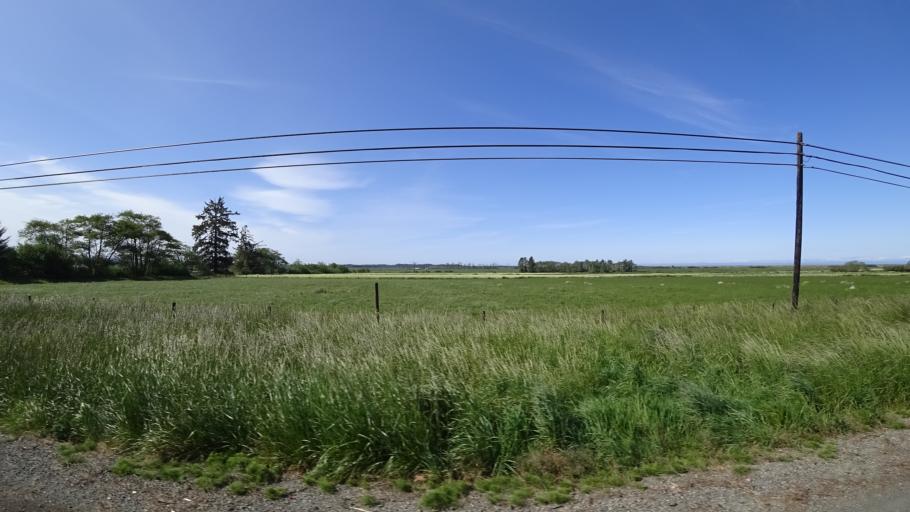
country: US
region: Oregon
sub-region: Curry County
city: Harbor
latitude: 41.9373
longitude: -124.1763
